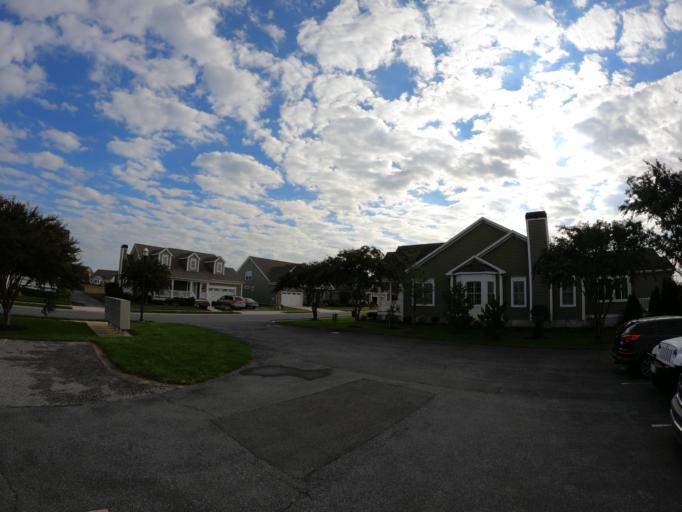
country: US
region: Delaware
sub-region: Sussex County
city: Lewes
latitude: 38.7551
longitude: -75.1679
